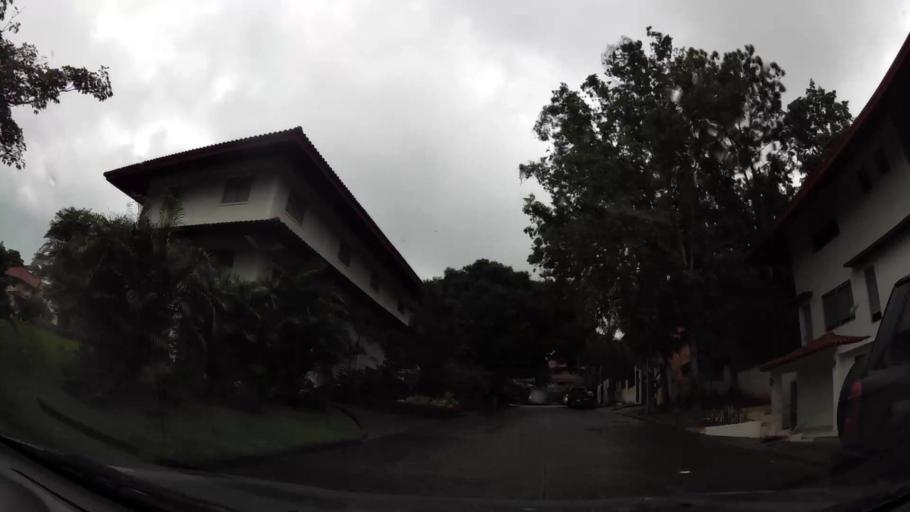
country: PA
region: Panama
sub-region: Distrito de Panama
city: Ancon
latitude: 8.9858
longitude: -79.5582
